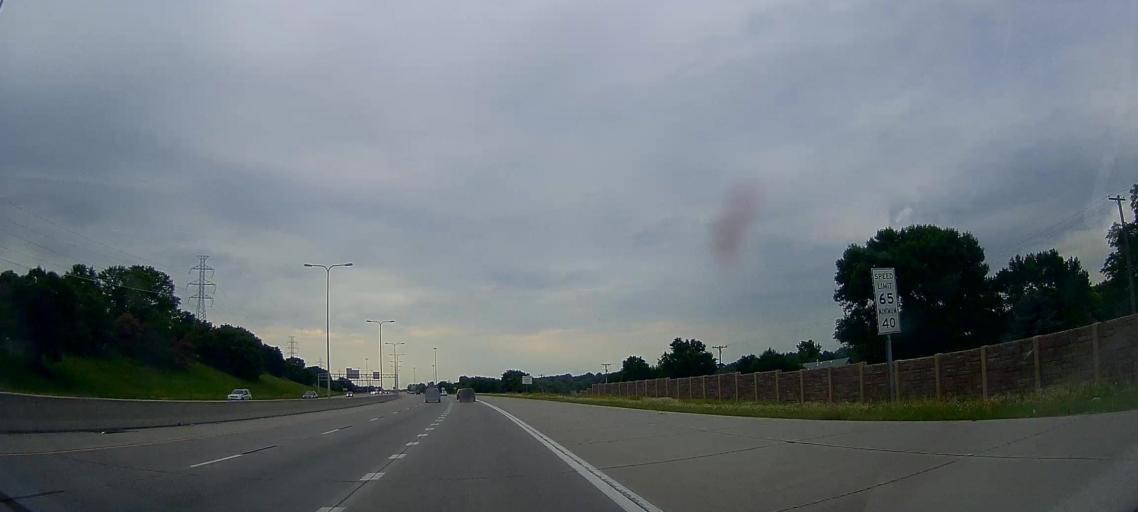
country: US
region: Nebraska
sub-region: Douglas County
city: Ralston
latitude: 41.2980
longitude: -96.0712
